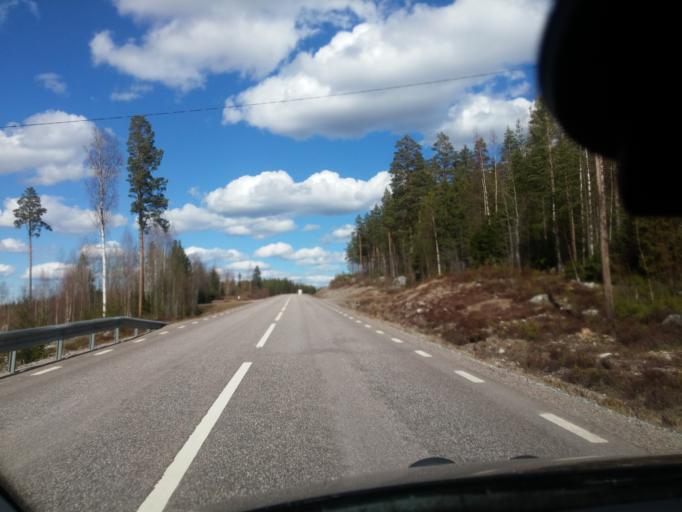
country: SE
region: Gaevleborg
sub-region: Ovanakers Kommun
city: Edsbyn
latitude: 61.2424
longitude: 15.8830
